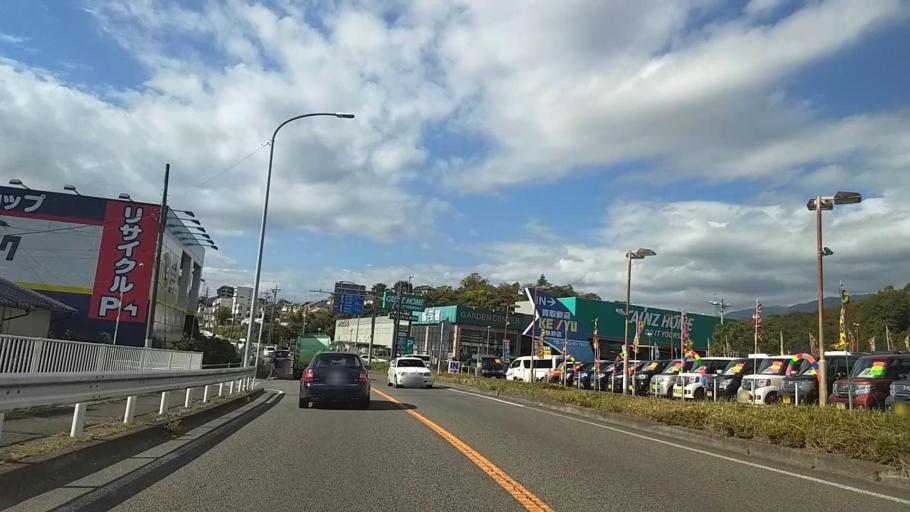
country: JP
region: Kanagawa
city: Hadano
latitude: 35.3812
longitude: 139.2295
